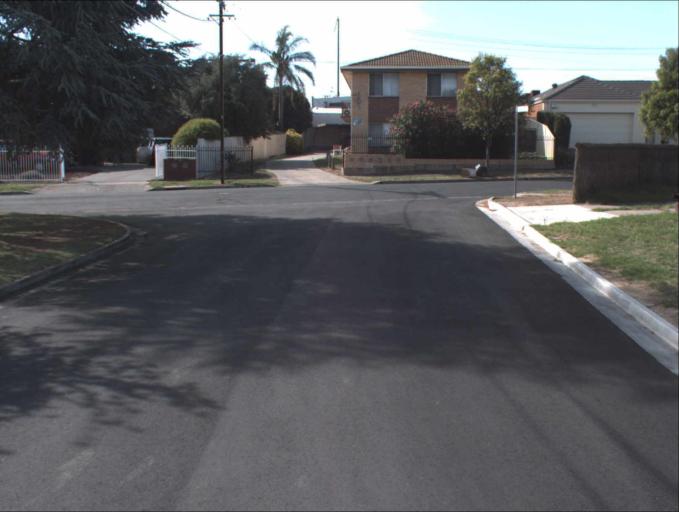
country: AU
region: South Australia
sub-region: Port Adelaide Enfield
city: Klemzig
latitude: -34.8739
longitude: 138.6359
